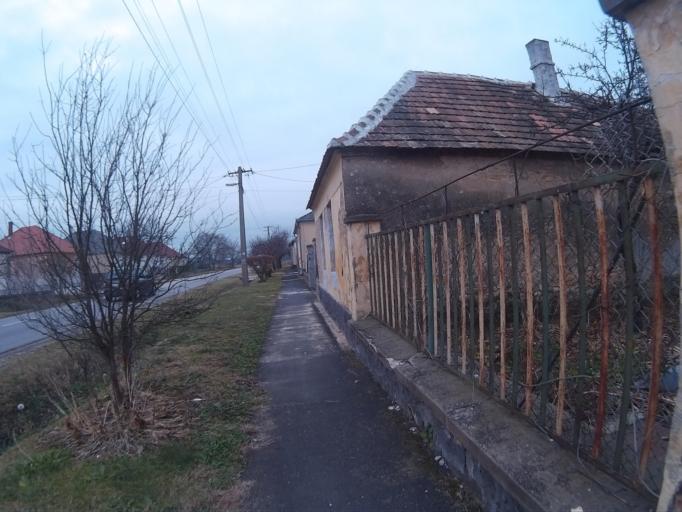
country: HU
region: Veszprem
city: Devecser
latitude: 46.9994
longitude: 17.4561
